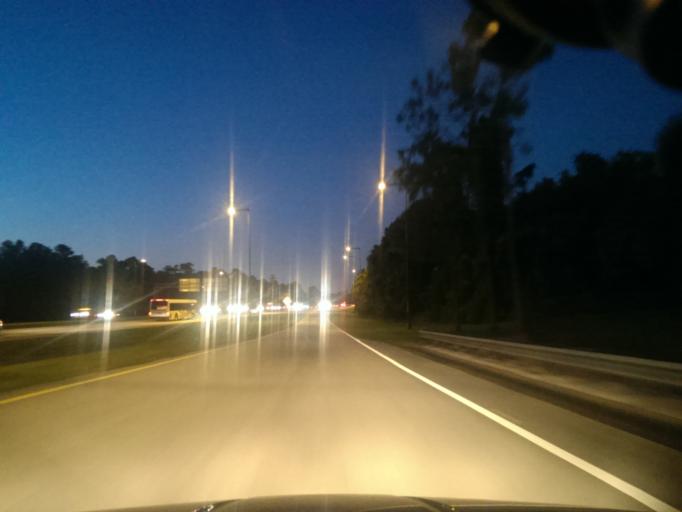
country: US
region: Florida
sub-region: Osceola County
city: Celebration
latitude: 28.3650
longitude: -81.5633
